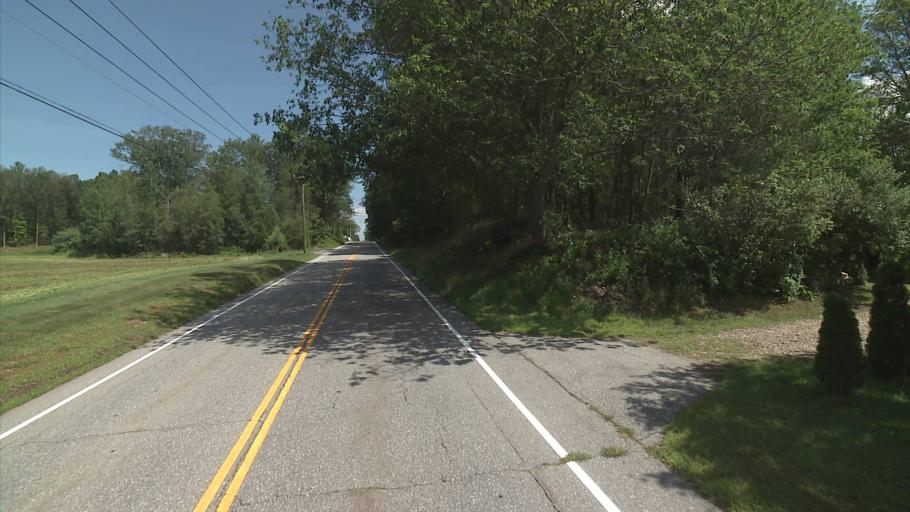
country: US
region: Connecticut
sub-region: Windham County
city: South Woodstock
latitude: 41.8712
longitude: -72.0891
